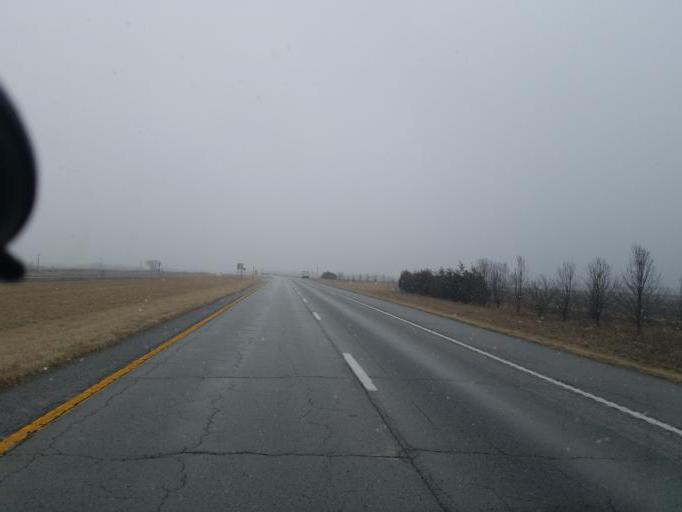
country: US
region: Missouri
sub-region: Macon County
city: La Plata
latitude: 39.9420
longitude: -92.4772
